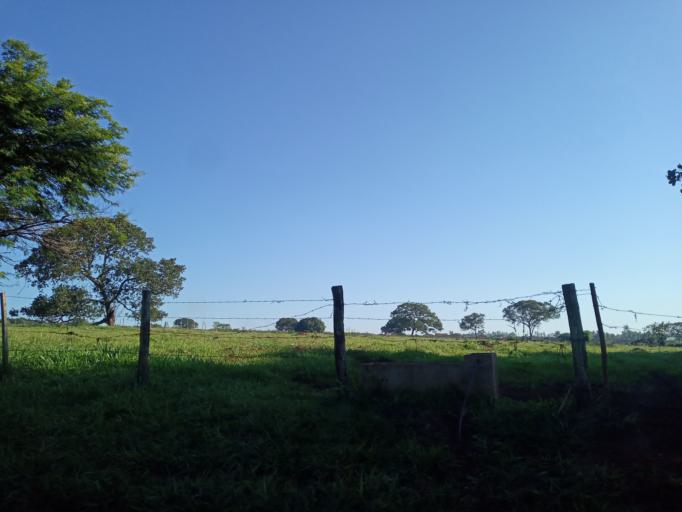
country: BR
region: Minas Gerais
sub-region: Ituiutaba
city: Ituiutaba
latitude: -18.9752
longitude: -49.4948
